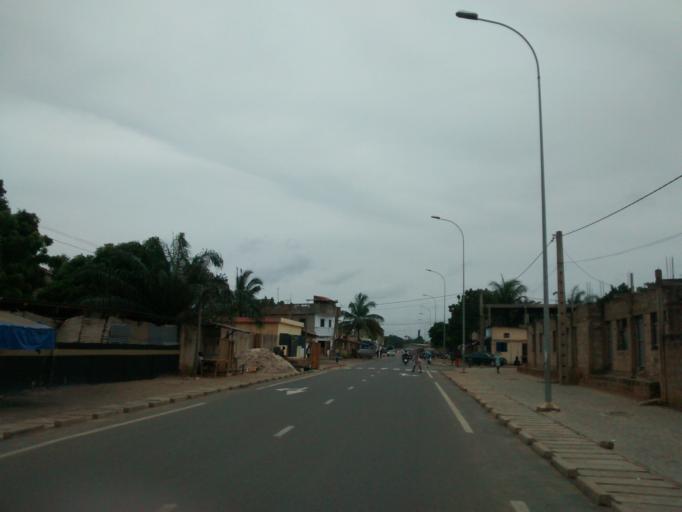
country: TG
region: Maritime
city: Lome
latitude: 6.2107
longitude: 1.1872
